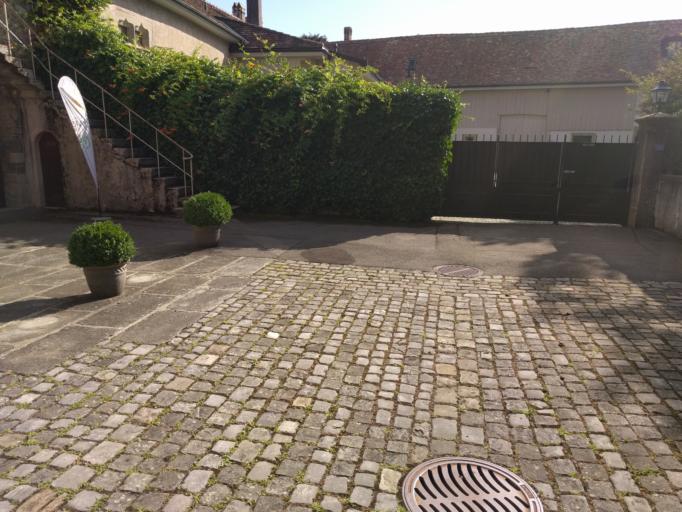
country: CH
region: Vaud
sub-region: Ouest Lausannois District
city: Ecublens
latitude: 46.5091
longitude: 6.5598
